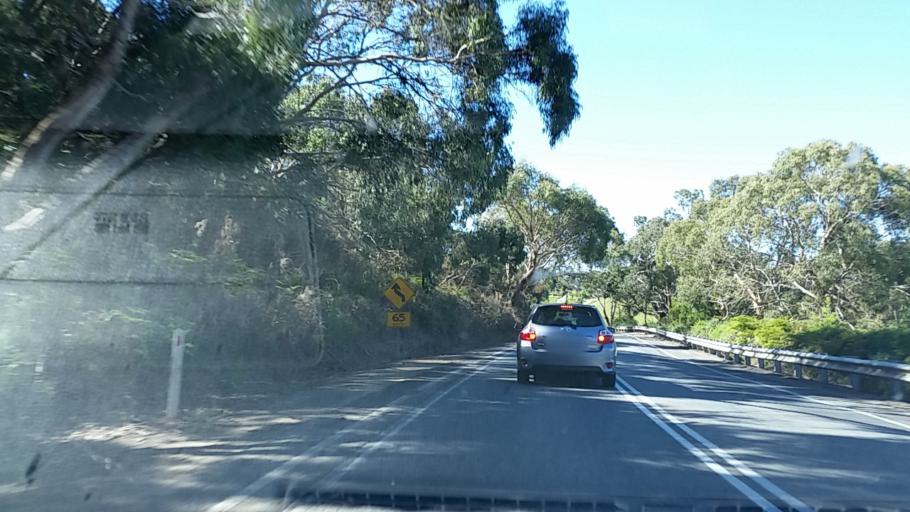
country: AU
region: South Australia
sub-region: Mount Barker
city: Meadows
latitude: -35.1878
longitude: 138.7714
